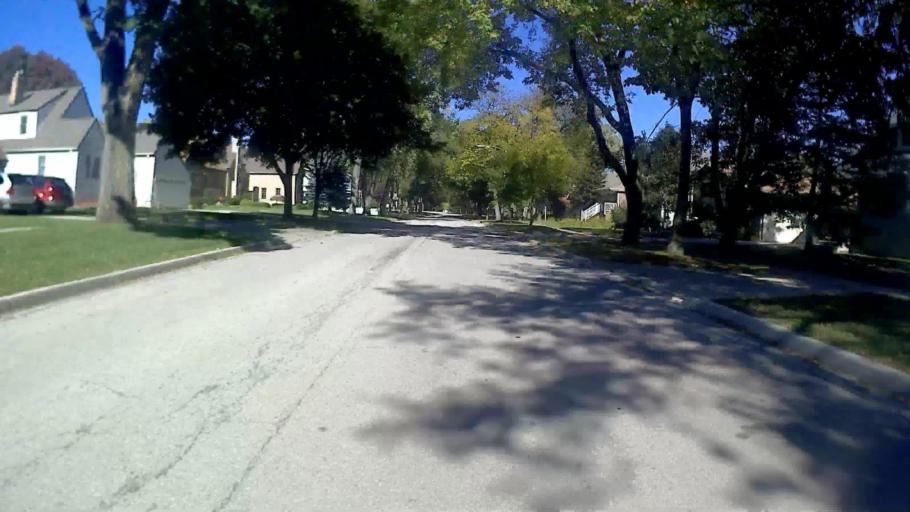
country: US
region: Illinois
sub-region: DuPage County
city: Itasca
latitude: 41.9665
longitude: -88.0146
